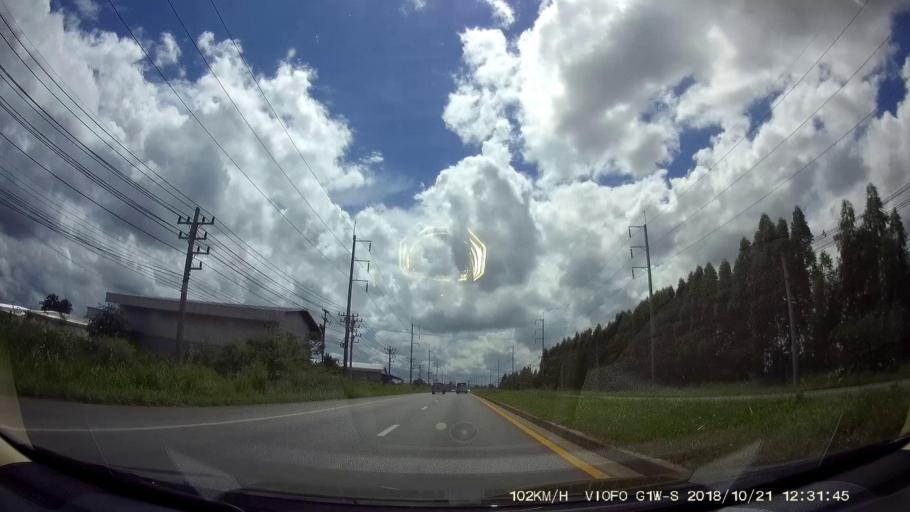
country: TH
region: Nakhon Ratchasima
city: Dan Khun Thot
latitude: 15.1518
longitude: 101.7335
